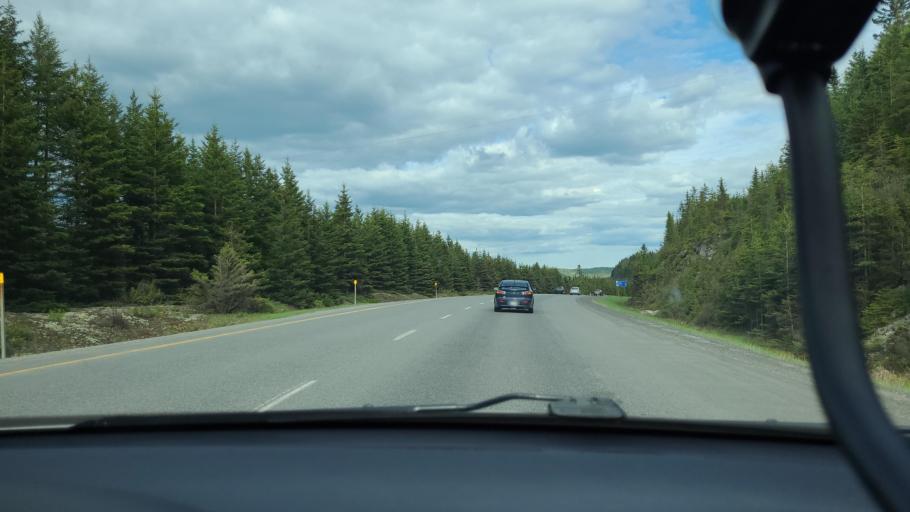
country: CA
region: Quebec
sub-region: Laurentides
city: Sainte-Agathe-des-Monts
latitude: 46.1043
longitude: -74.4012
